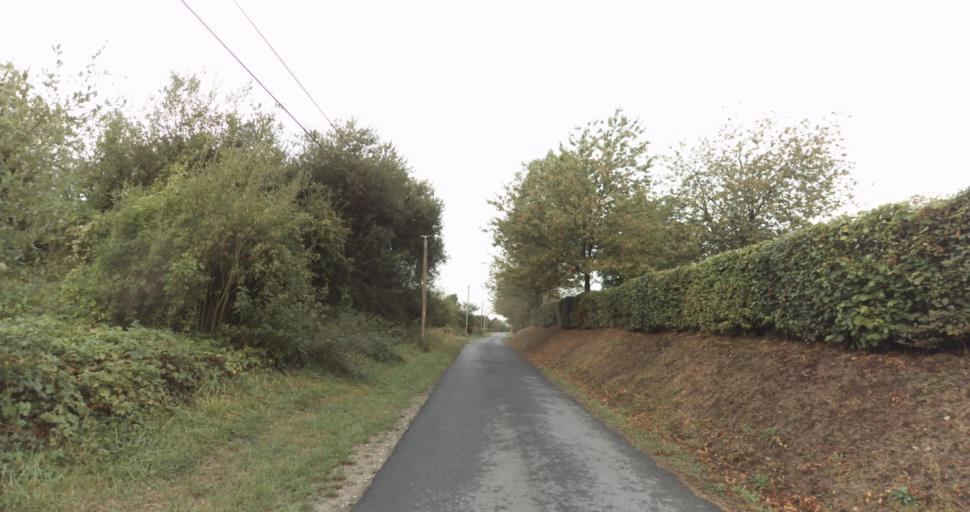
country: FR
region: Lower Normandy
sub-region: Departement de l'Orne
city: Vimoutiers
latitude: 48.9155
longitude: 0.2175
